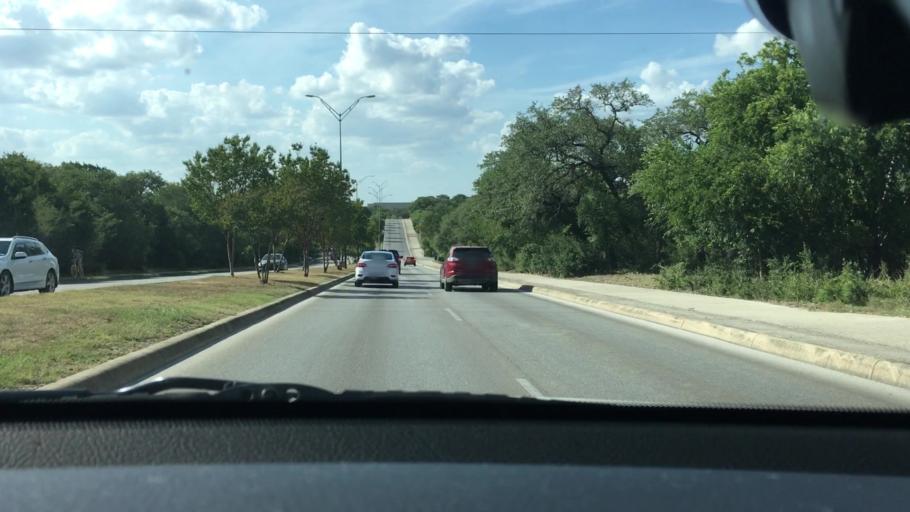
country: US
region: Texas
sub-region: Bexar County
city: Selma
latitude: 29.5852
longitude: -98.2868
